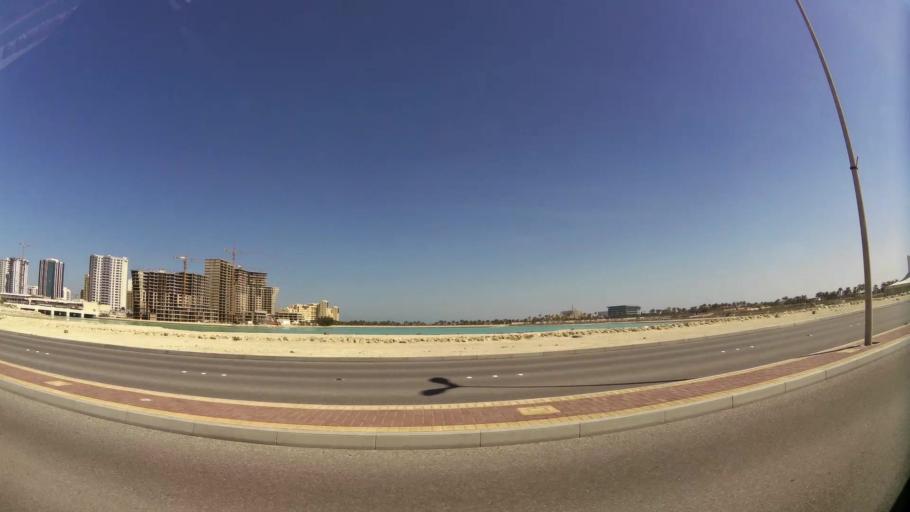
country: BH
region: Muharraq
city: Al Hadd
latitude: 26.2843
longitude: 50.6588
